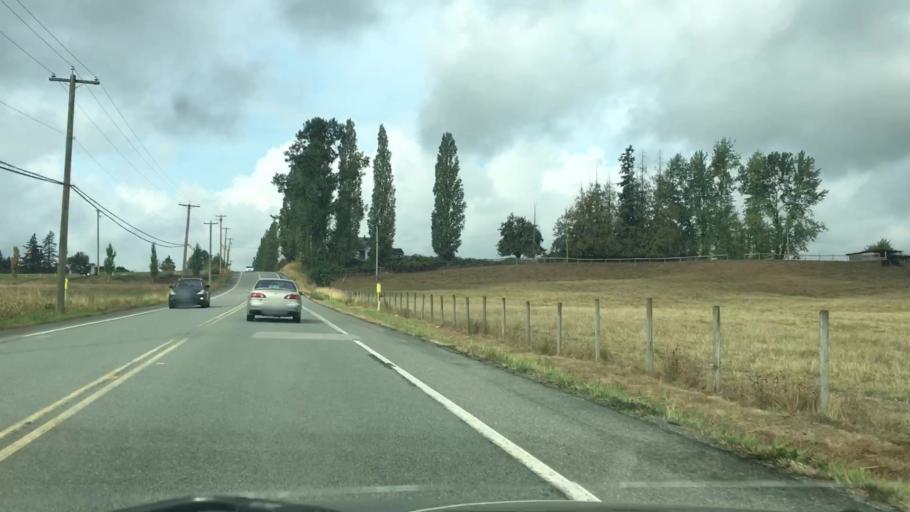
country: CA
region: British Columbia
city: Langley
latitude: 49.1044
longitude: -122.5907
